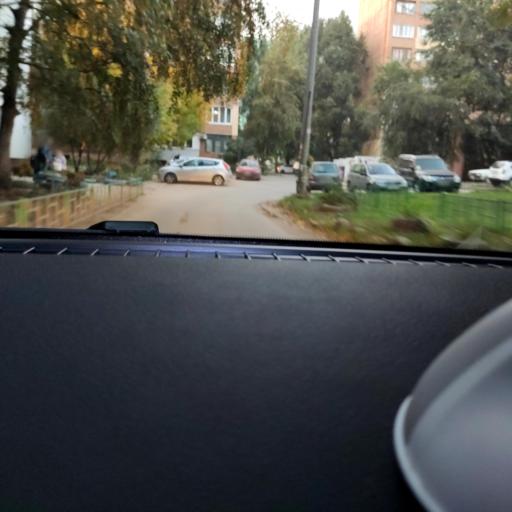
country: RU
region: Samara
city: Samara
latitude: 53.2328
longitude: 50.2590
